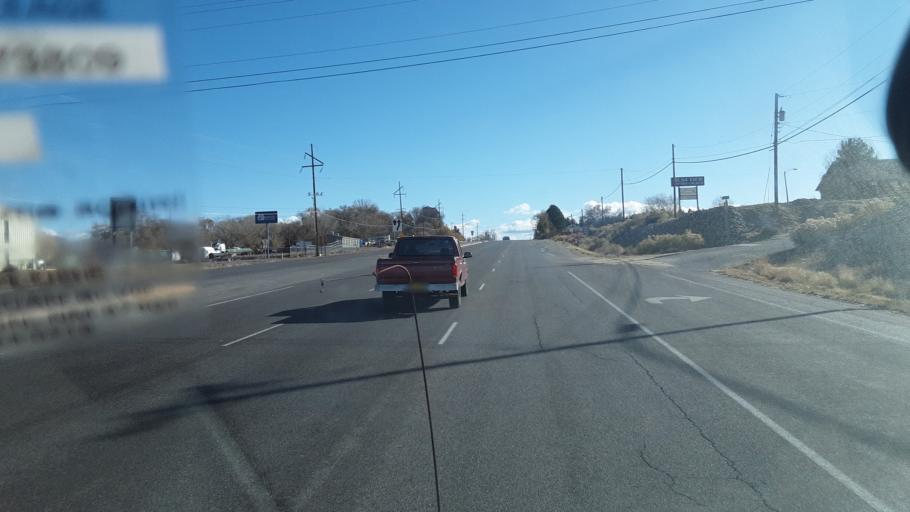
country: US
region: New Mexico
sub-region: San Juan County
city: Lee Acres
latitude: 36.7010
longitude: -108.0606
